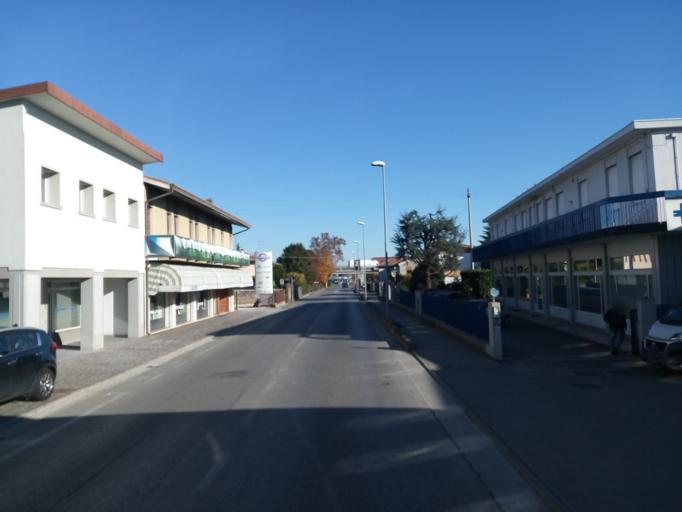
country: IT
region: Veneto
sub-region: Provincia di Treviso
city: Montebelluna
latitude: 45.7798
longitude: 12.0644
